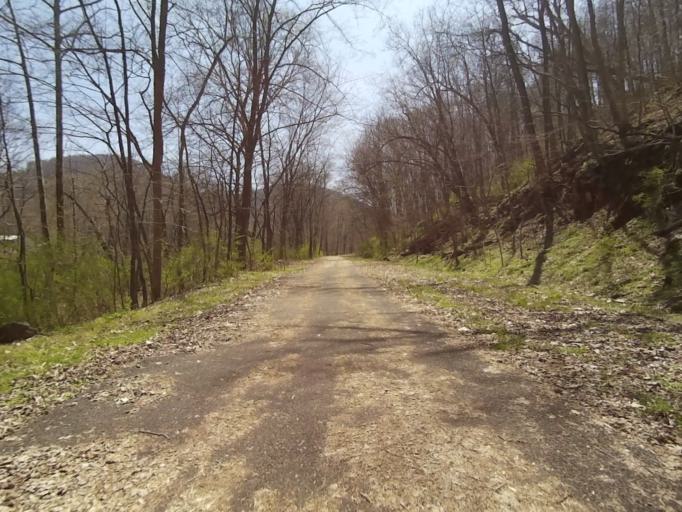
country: US
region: Pennsylvania
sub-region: Blair County
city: Williamsburg
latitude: 40.4827
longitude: -78.1751
